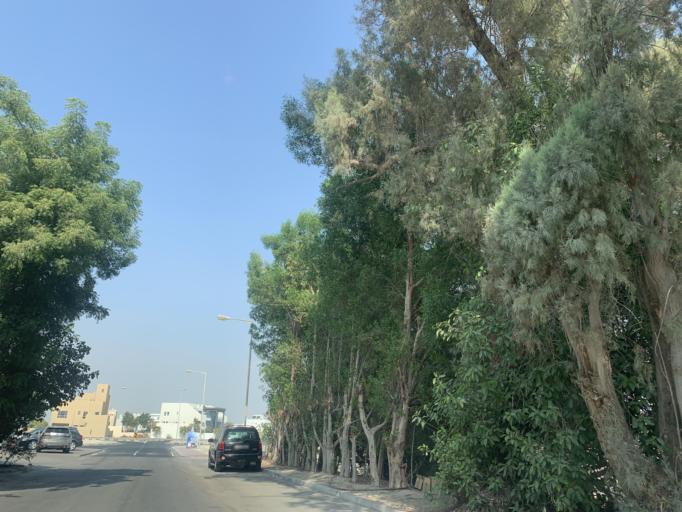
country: BH
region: Central Governorate
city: Madinat Hamad
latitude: 26.1292
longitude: 50.4913
